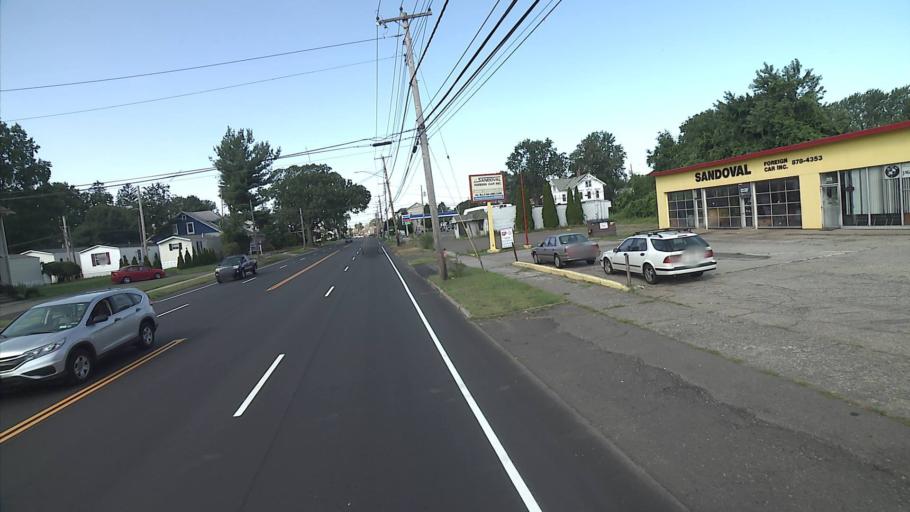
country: US
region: Connecticut
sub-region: Fairfield County
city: Stratford
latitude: 41.2038
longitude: -73.0976
